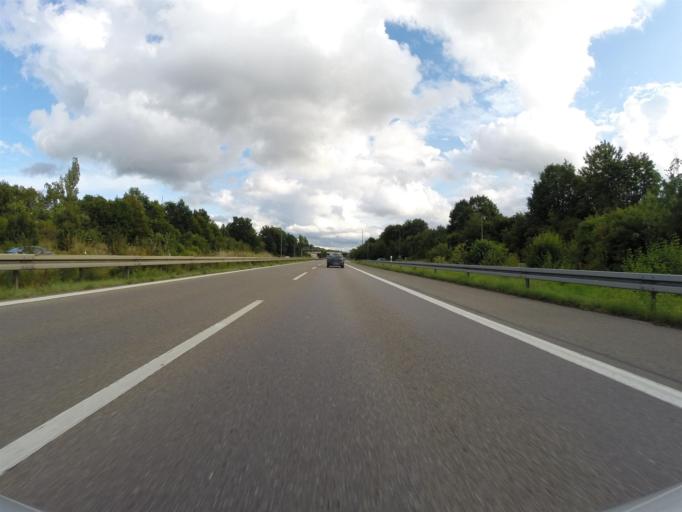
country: DE
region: Bavaria
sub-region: Regierungsbezirk Mittelfranken
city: Nuernberg
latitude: 49.4107
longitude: 11.0687
